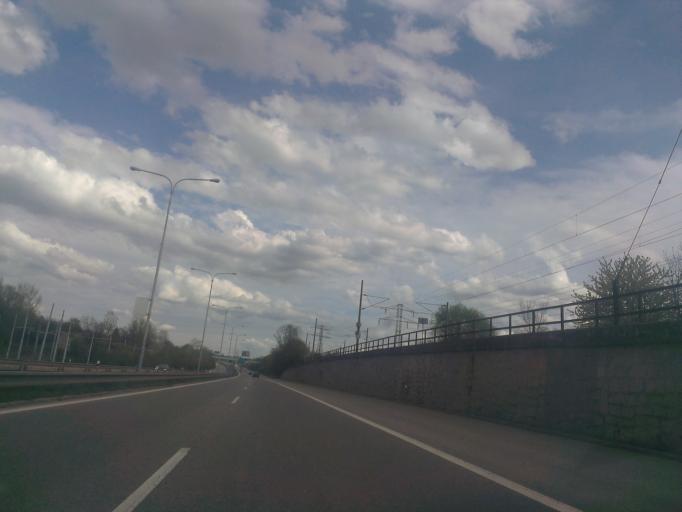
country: CZ
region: South Moravian
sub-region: Mesto Brno
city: Brno
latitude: 49.1876
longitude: 16.6564
